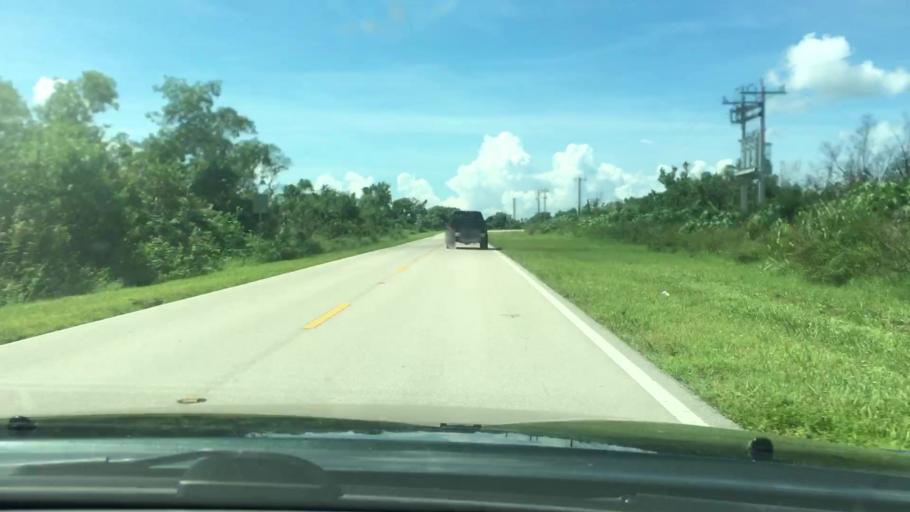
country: US
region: Florida
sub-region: Collier County
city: Marco
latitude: 25.9372
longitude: -81.6474
